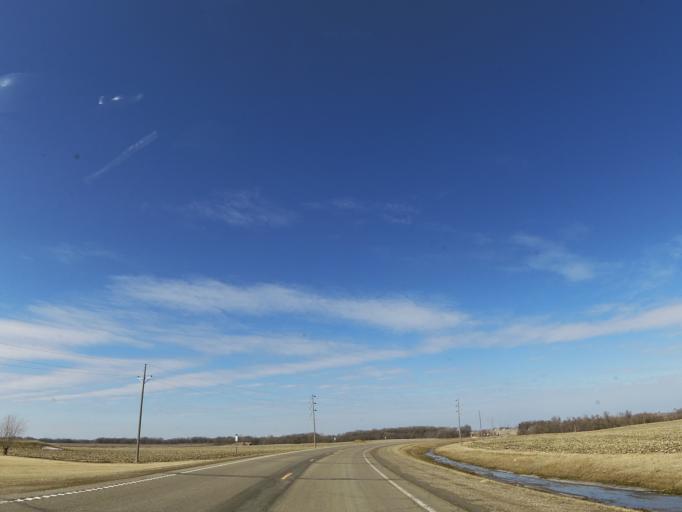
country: US
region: Minnesota
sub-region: Waseca County
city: New Richland
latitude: 43.9378
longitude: -93.4906
